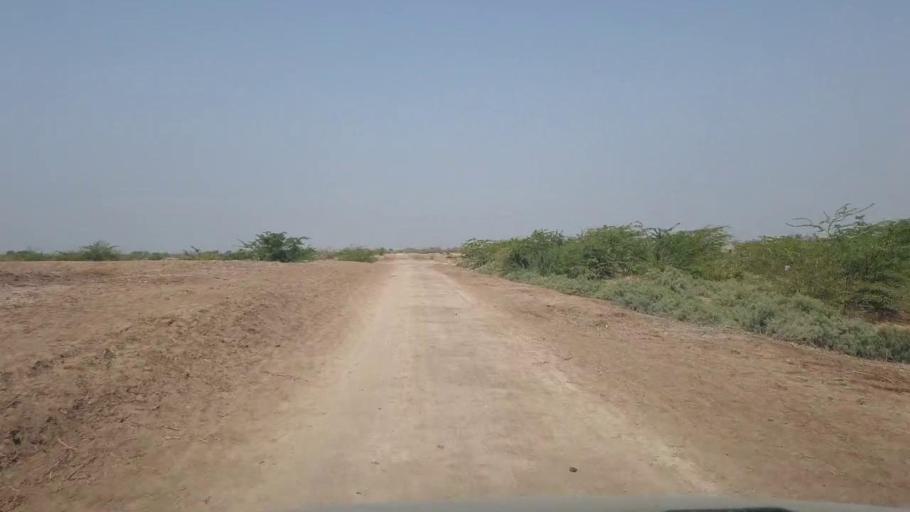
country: PK
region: Sindh
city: Chor
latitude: 25.4678
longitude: 69.7636
